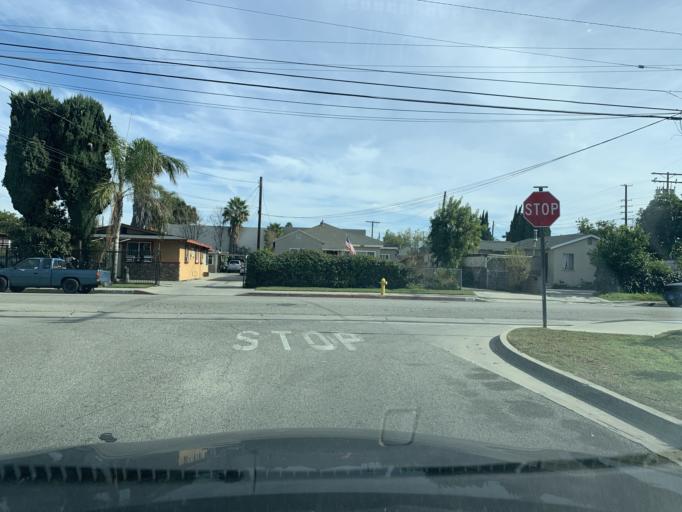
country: US
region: California
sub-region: Los Angeles County
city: South El Monte
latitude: 34.0527
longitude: -118.0559
